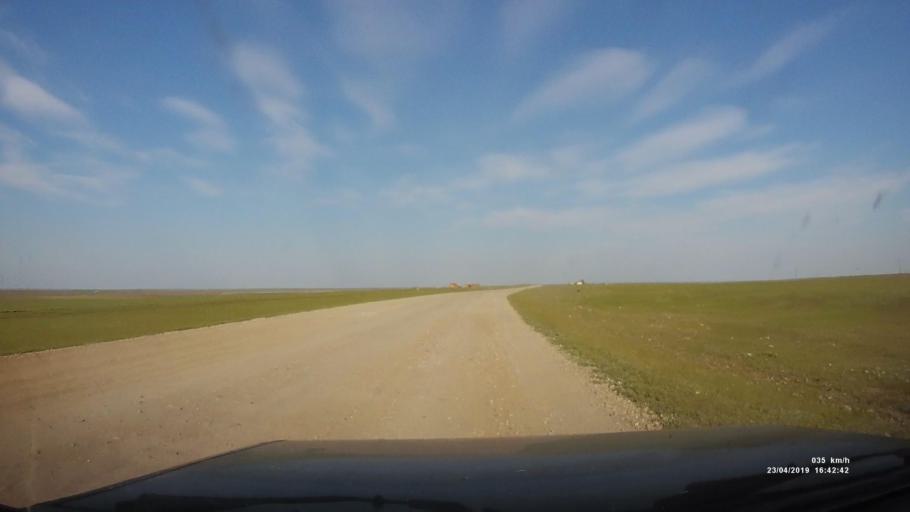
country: RU
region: Kalmykiya
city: Priyutnoye
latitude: 46.3479
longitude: 43.1956
